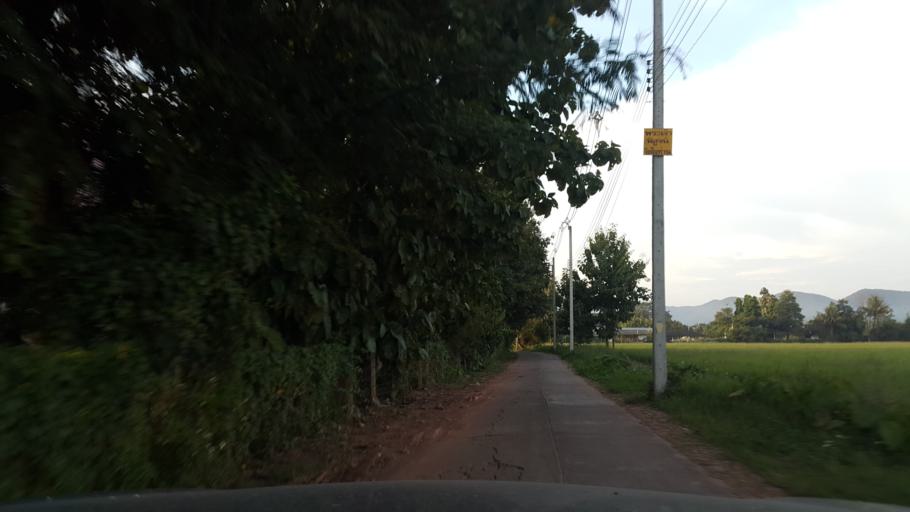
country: TH
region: Chiang Mai
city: San Sai
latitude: 18.8882
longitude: 99.0850
